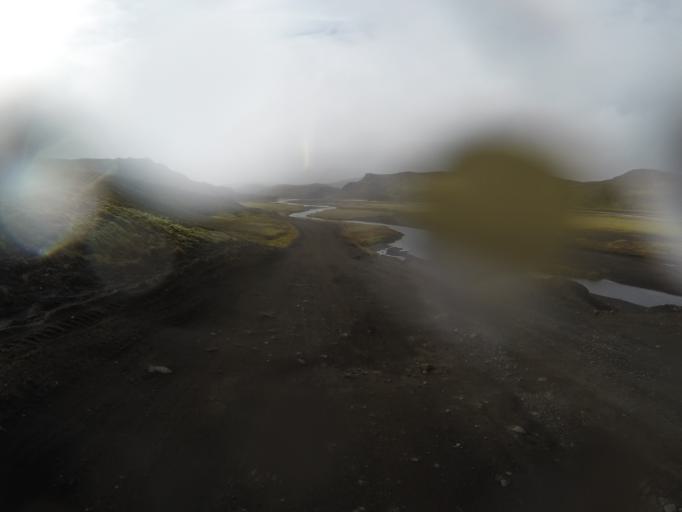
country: IS
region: South
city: Vestmannaeyjar
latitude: 63.9828
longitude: -18.8566
